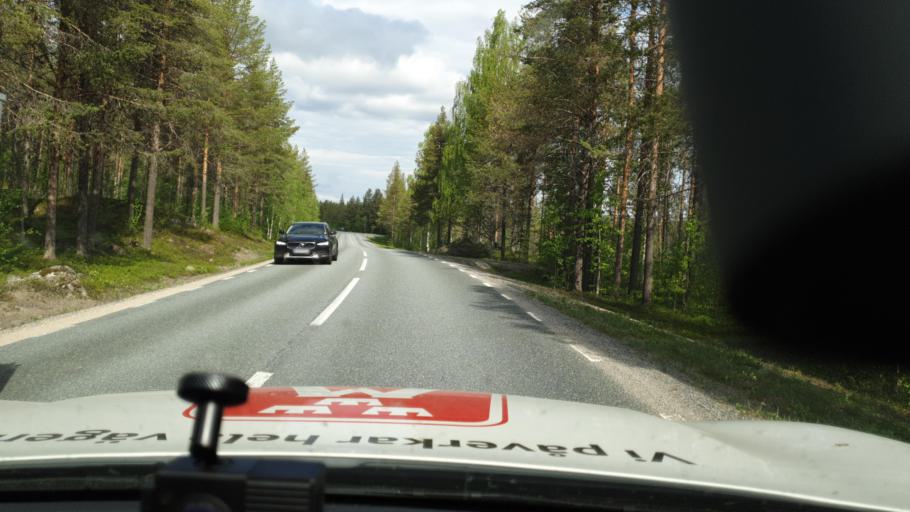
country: SE
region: Vaesterbotten
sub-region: Sorsele Kommun
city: Sorsele
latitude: 65.4832
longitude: 17.5639
